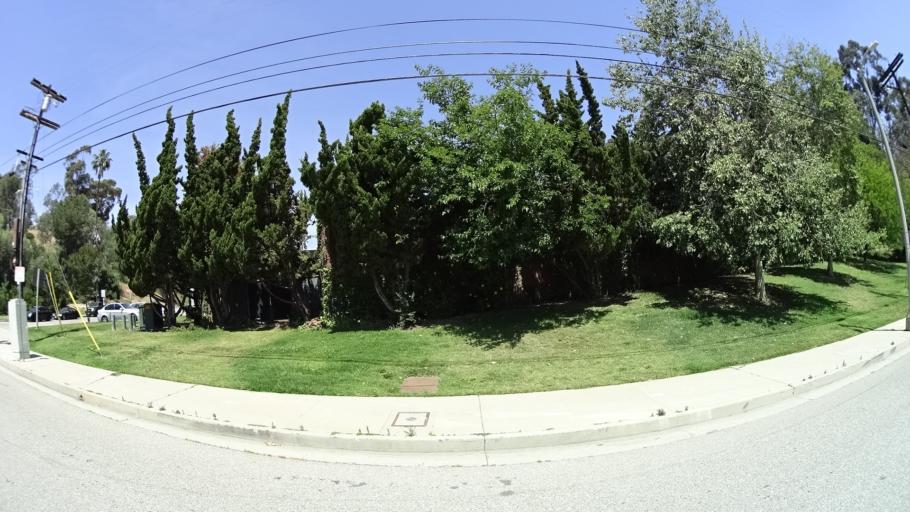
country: US
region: California
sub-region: Los Angeles County
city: Echo Park
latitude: 34.0795
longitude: -118.2357
